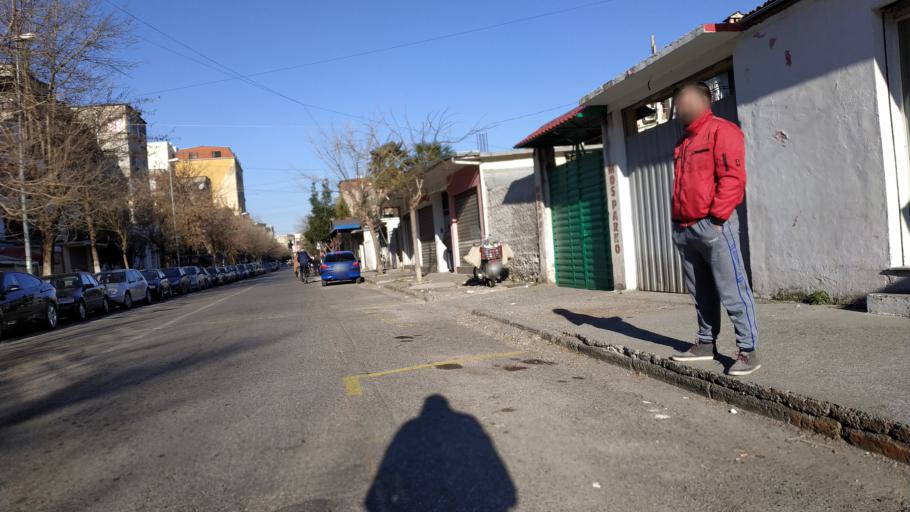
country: AL
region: Shkoder
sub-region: Rrethi i Shkodres
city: Shkoder
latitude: 42.0625
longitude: 19.5113
